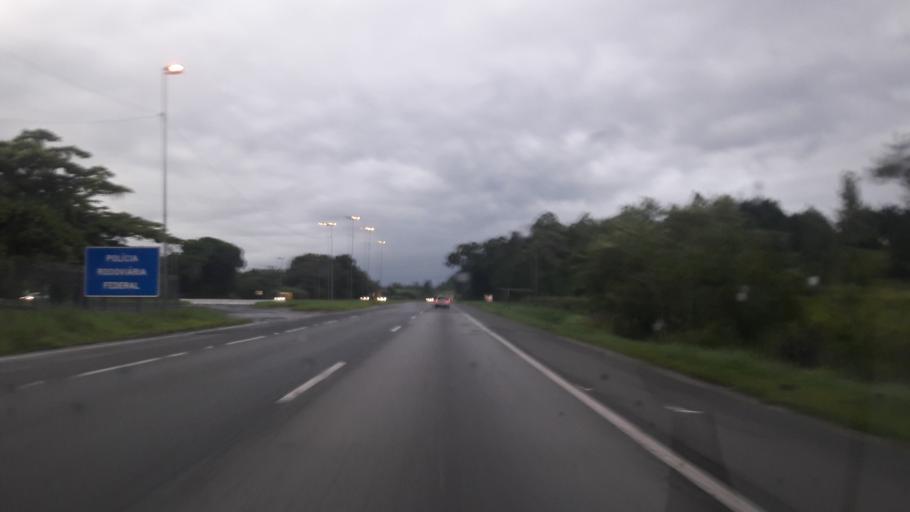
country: BR
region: Sao Paulo
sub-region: Cajati
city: Cajati
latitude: -24.7770
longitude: -48.1702
